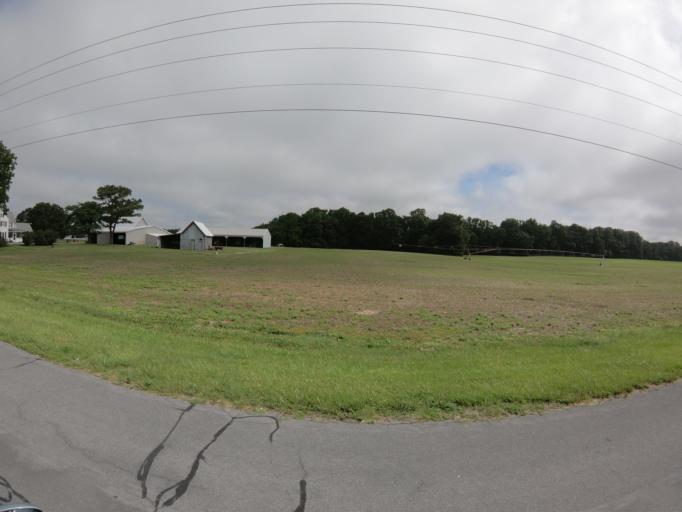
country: US
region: Delaware
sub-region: Kent County
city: Felton
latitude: 39.0066
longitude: -75.5504
